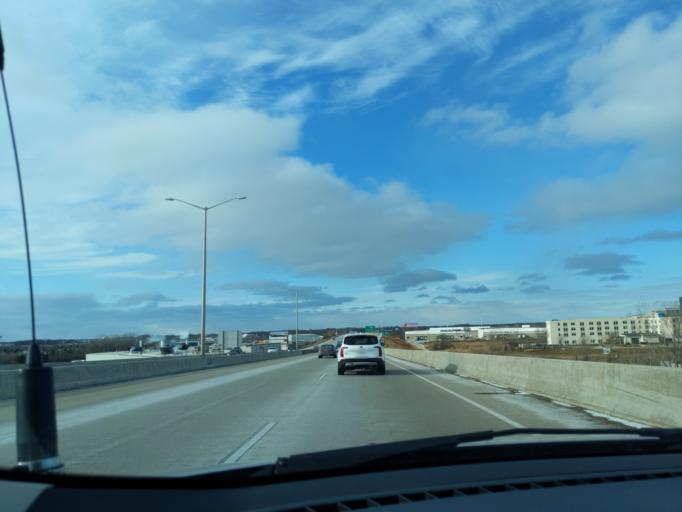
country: US
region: Wisconsin
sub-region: Brown County
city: Ashwaubenon
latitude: 44.4767
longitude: -88.0481
